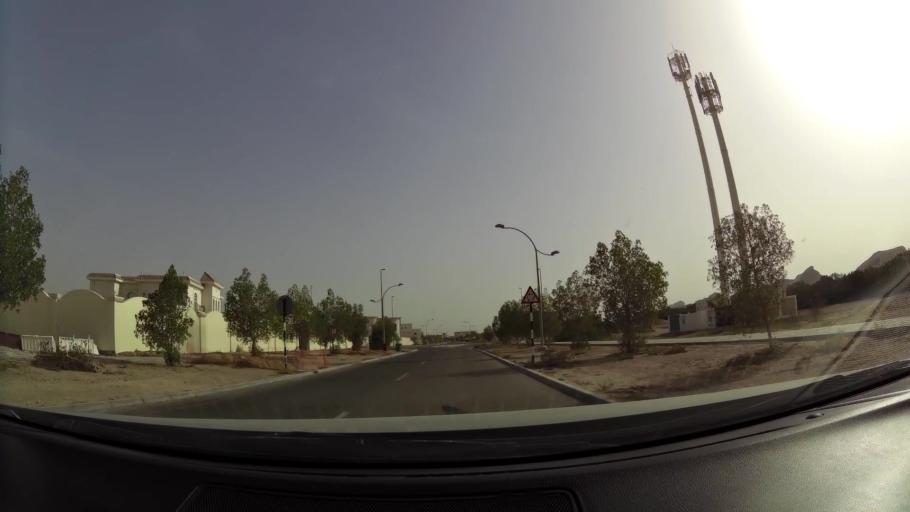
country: AE
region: Abu Dhabi
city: Al Ain
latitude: 24.1374
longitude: 55.7239
